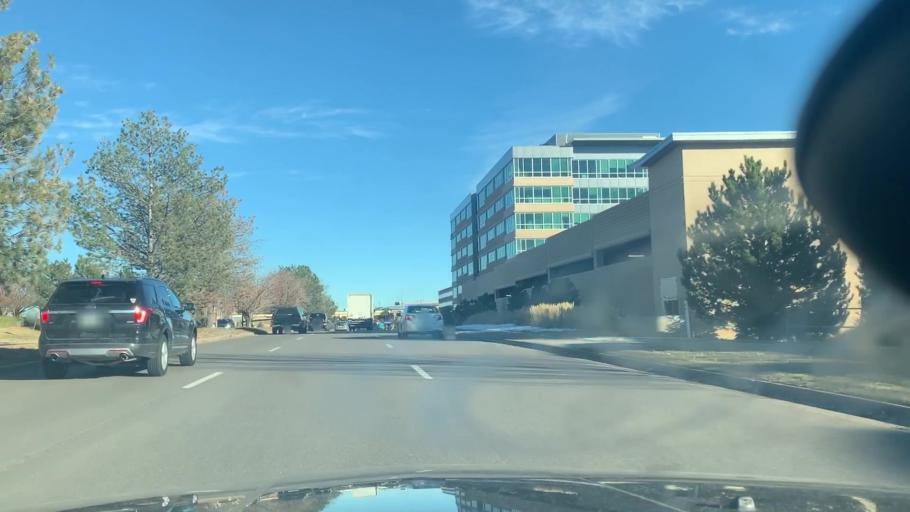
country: US
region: Colorado
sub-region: Arapahoe County
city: Centennial
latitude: 39.5805
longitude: -104.8839
